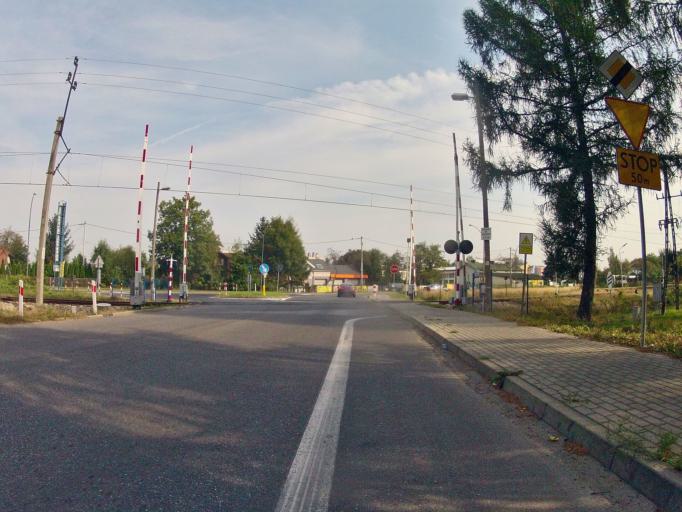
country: PL
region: Subcarpathian Voivodeship
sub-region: Powiat jasielski
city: Jaslo
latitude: 49.7254
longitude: 21.4491
